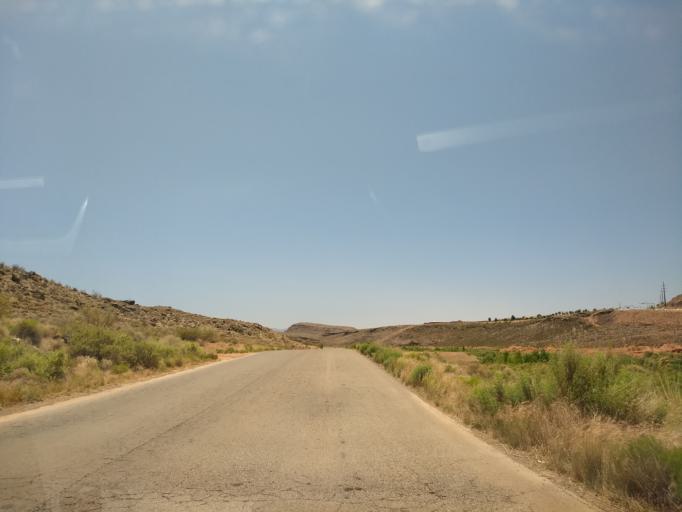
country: US
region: Utah
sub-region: Washington County
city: Washington
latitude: 37.1401
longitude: -113.4598
